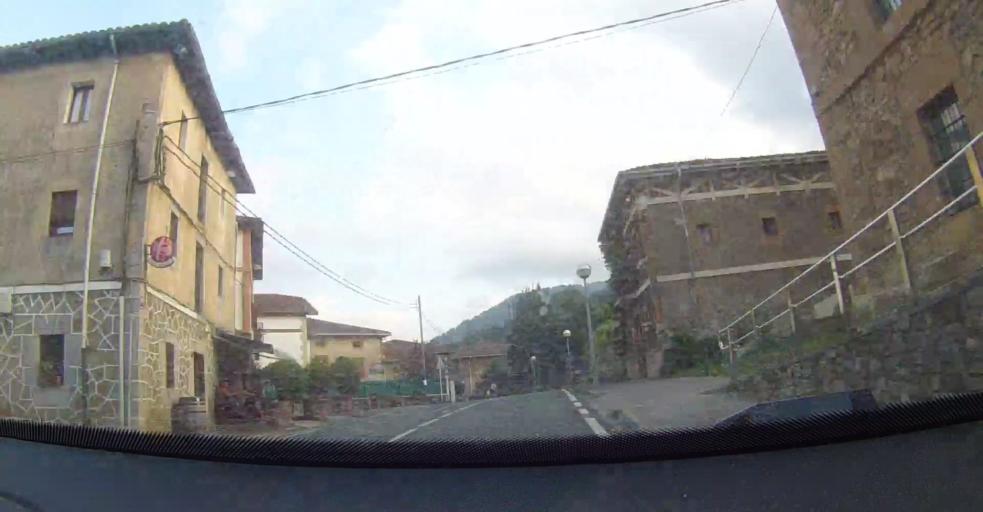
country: ES
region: Basque Country
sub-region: Bizkaia
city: Sopuerta
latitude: 43.2615
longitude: -3.1540
